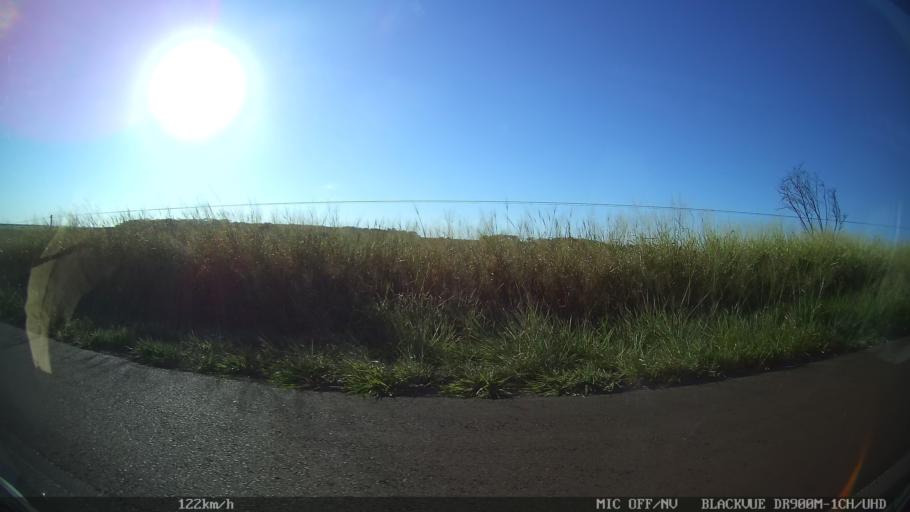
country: BR
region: Sao Paulo
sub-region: Guapiacu
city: Guapiacu
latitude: -20.7412
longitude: -49.0980
